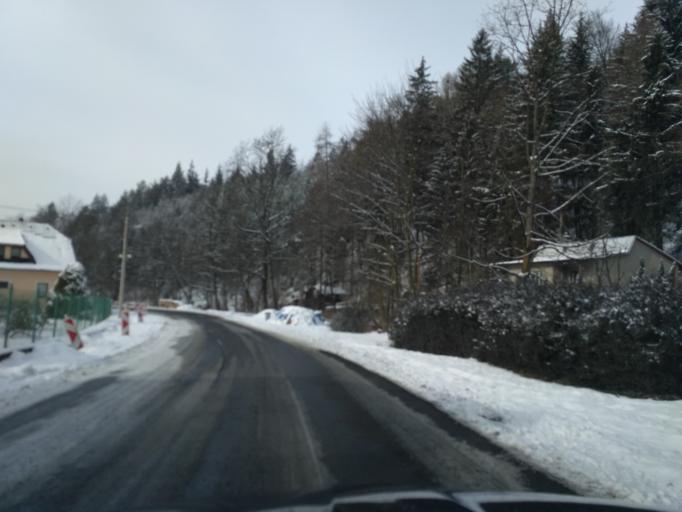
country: CZ
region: Zlin
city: Valasska Bystrice
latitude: 49.4199
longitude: 18.0957
